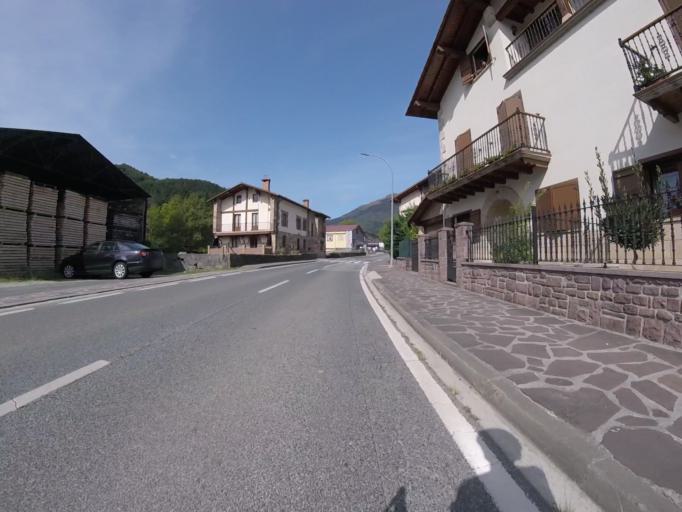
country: ES
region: Navarre
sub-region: Provincia de Navarra
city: Doneztebe
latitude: 43.1331
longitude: -1.6750
